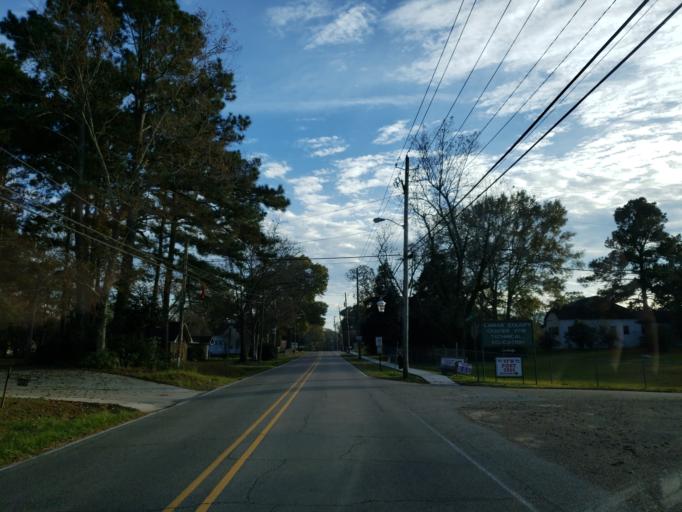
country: US
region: Mississippi
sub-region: Lamar County
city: Purvis
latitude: 31.1515
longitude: -89.4117
